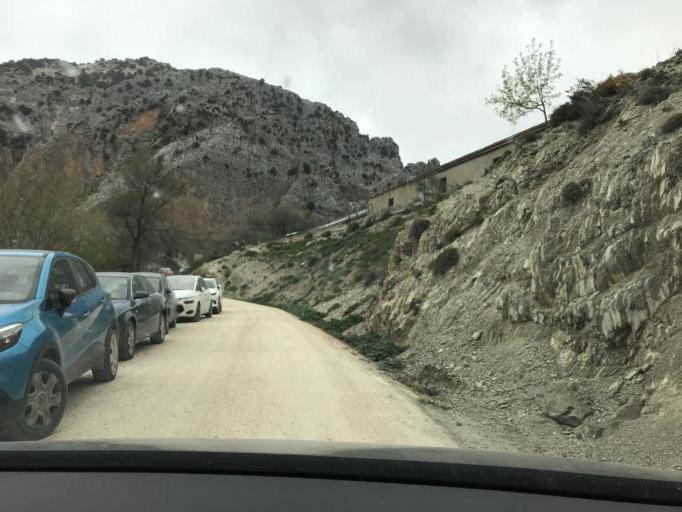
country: ES
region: Andalusia
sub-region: Provincia de Granada
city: Castril
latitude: 37.8904
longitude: -2.7496
